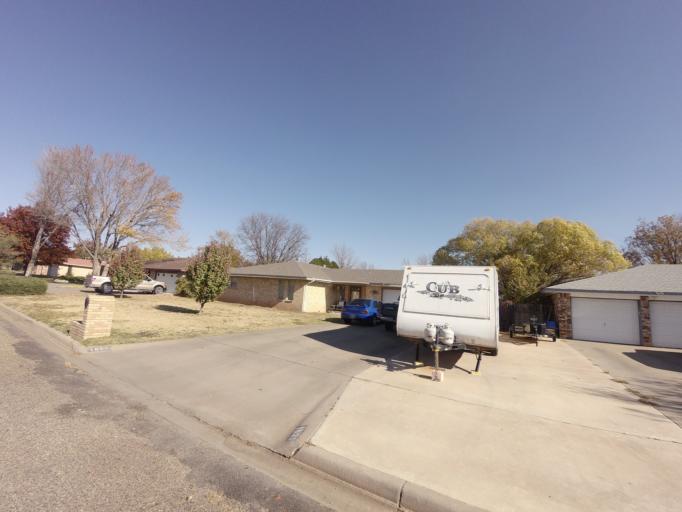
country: US
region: New Mexico
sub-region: Curry County
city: Clovis
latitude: 34.4150
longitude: -103.1825
